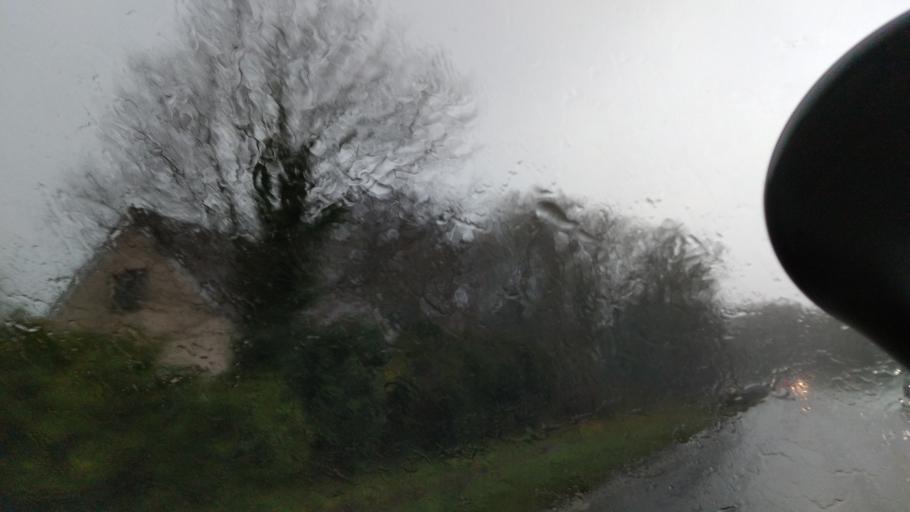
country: GB
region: England
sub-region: West Sussex
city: Arundel
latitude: 50.8557
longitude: -0.5781
